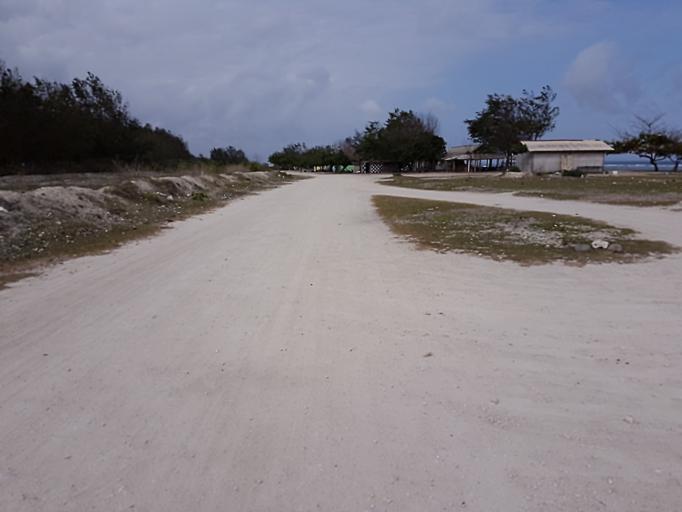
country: ID
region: Bali
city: Karyadharma
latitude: -8.7412
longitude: 115.2404
